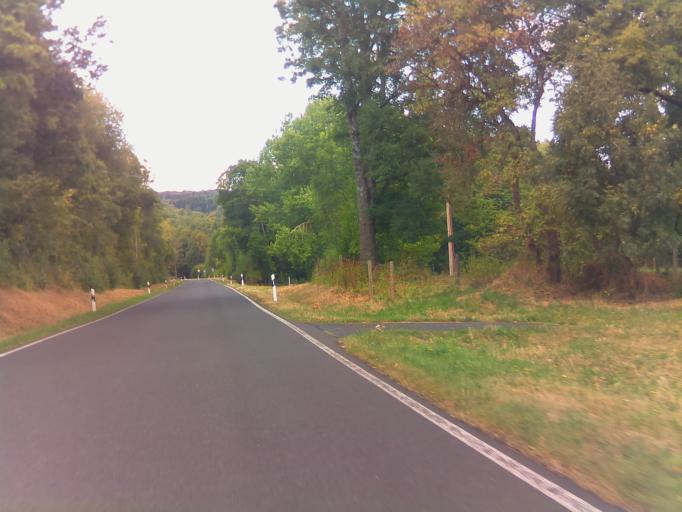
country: DE
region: Bavaria
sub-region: Regierungsbezirk Unterfranken
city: Oberelsbach
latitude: 50.4666
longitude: 10.1007
